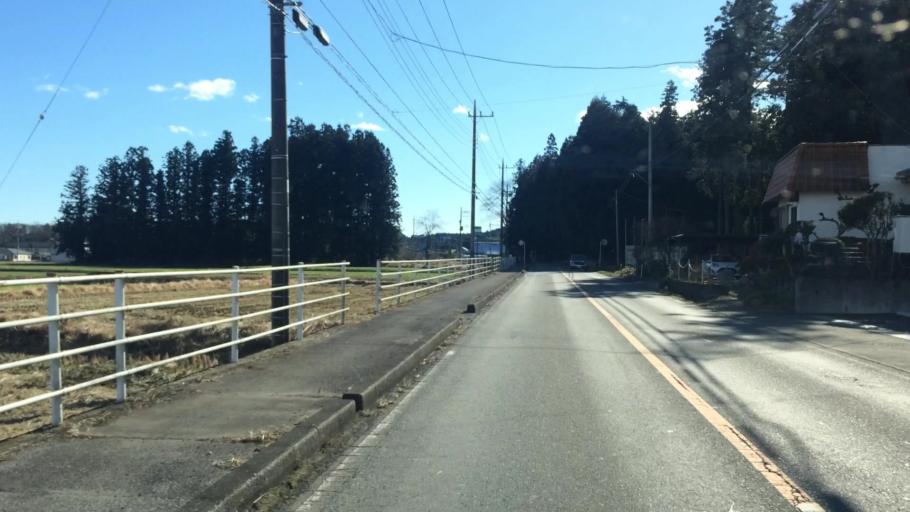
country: JP
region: Tochigi
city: Imaichi
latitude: 36.7514
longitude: 139.7337
